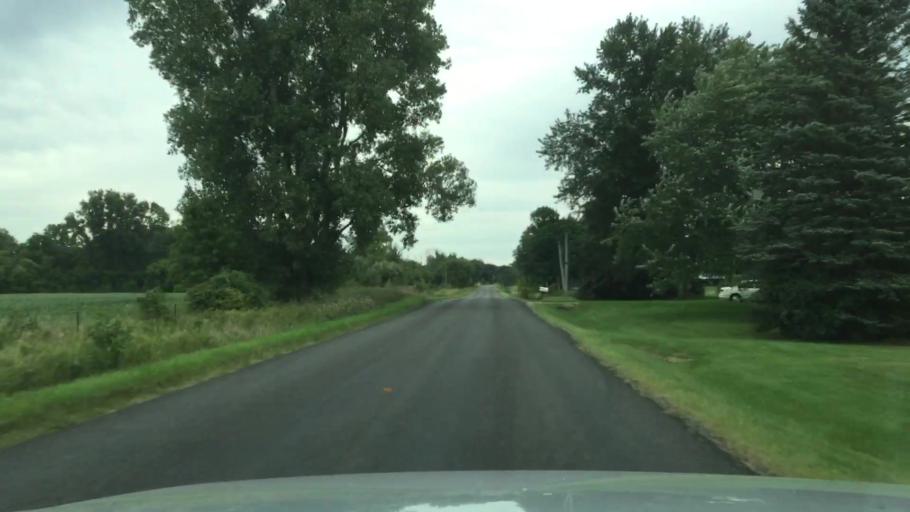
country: US
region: Michigan
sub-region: Shiawassee County
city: Durand
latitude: 42.8670
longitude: -84.0494
